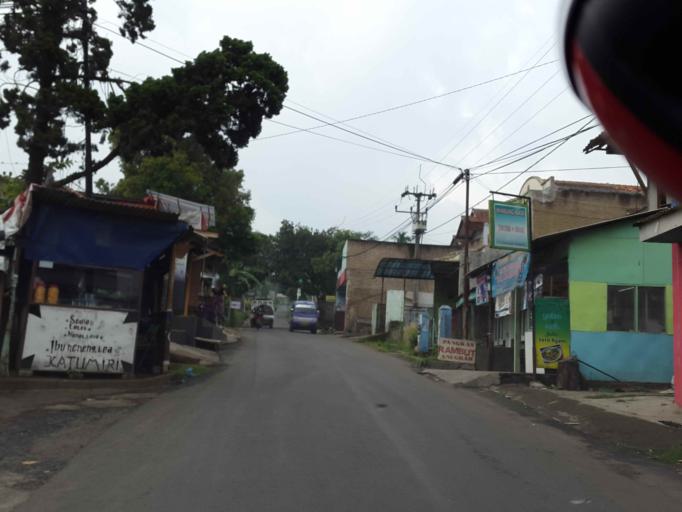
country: ID
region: West Java
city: Cimahi
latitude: -6.8384
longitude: 107.5737
